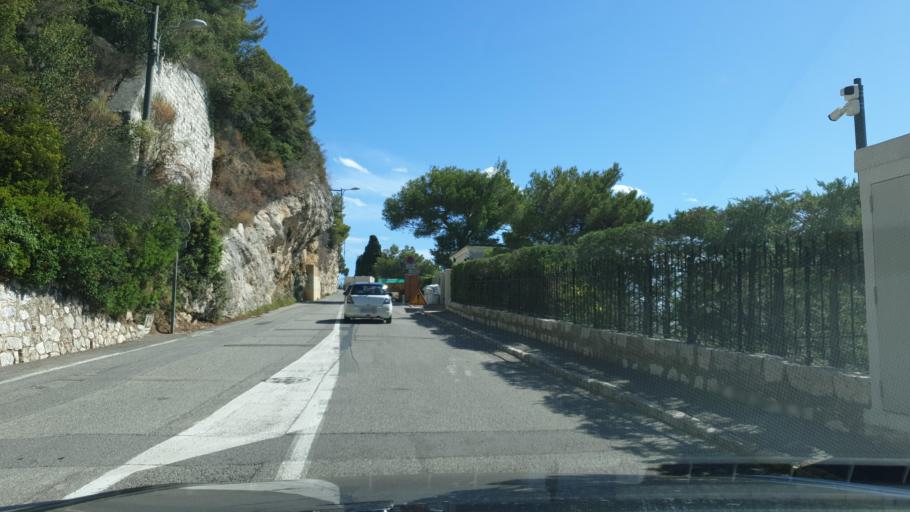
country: FR
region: Provence-Alpes-Cote d'Azur
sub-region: Departement des Alpes-Maritimes
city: Eze
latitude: 43.7195
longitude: 7.3710
